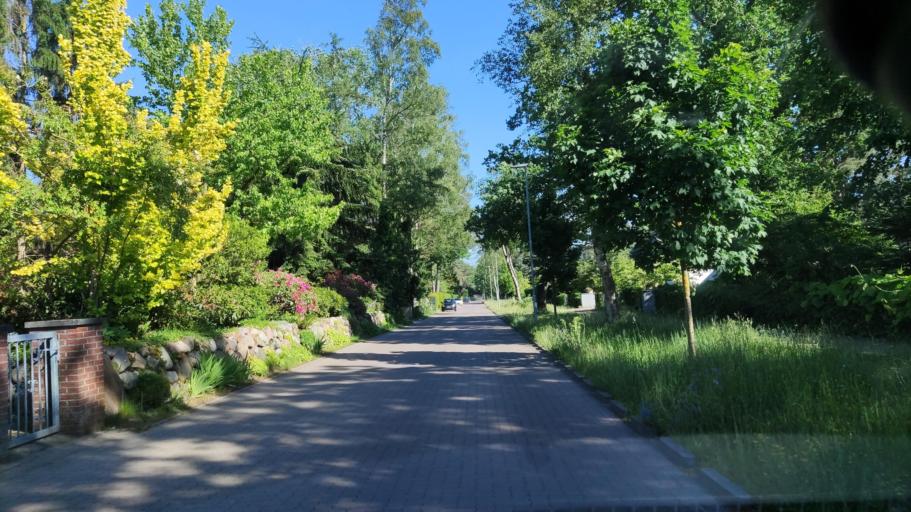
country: DE
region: Lower Saxony
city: Marxen
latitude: 53.3724
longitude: 10.0422
